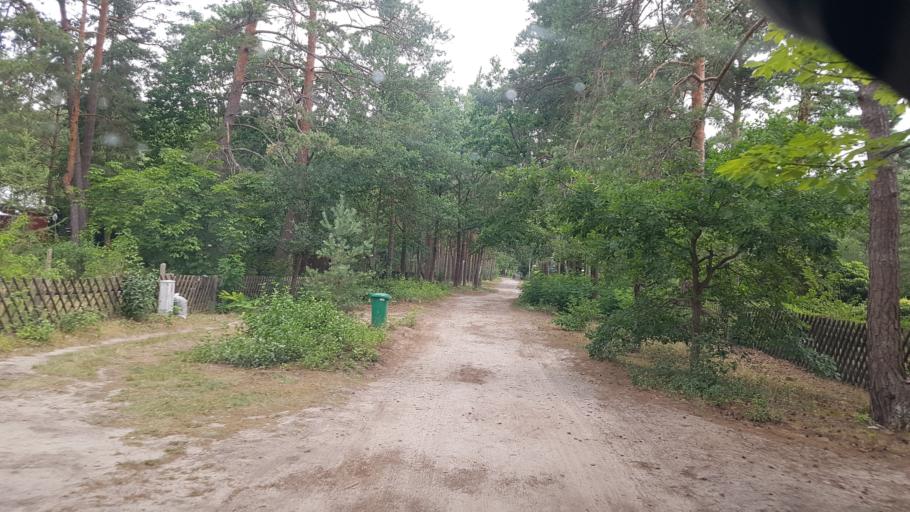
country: DE
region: Brandenburg
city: Gross Koris
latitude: 52.1604
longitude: 13.6969
